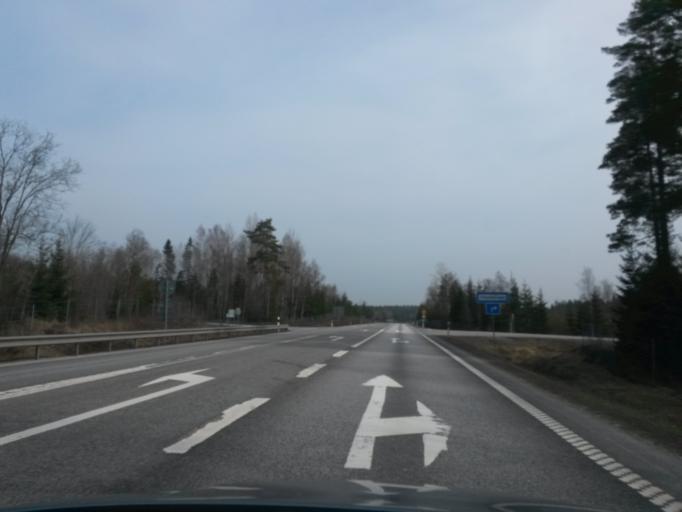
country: SE
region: Vaestra Goetaland
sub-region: Gullspangs Kommun
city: Anderstorp
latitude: 58.9014
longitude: 14.3394
